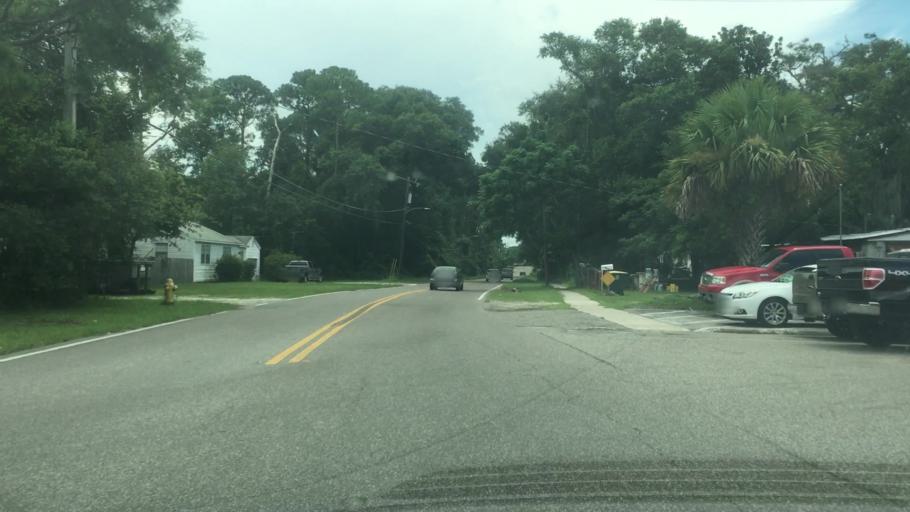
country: US
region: Florida
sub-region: Duval County
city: Jacksonville
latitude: 30.3198
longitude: -81.5469
